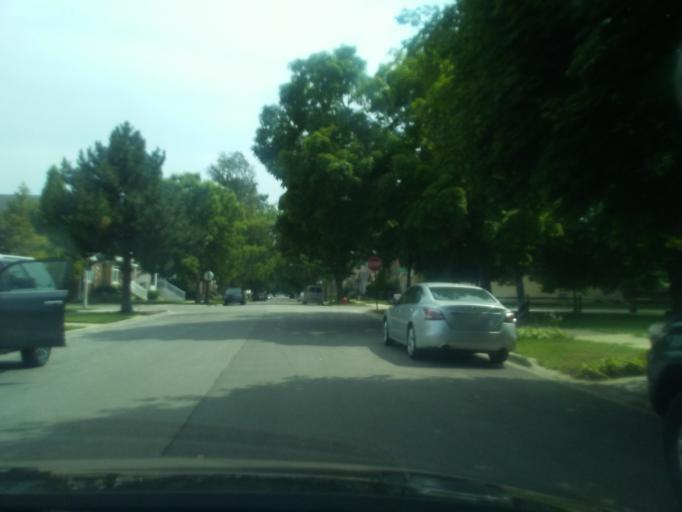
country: US
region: Illinois
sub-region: Cook County
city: Harwood Heights
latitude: 41.9806
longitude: -87.7939
